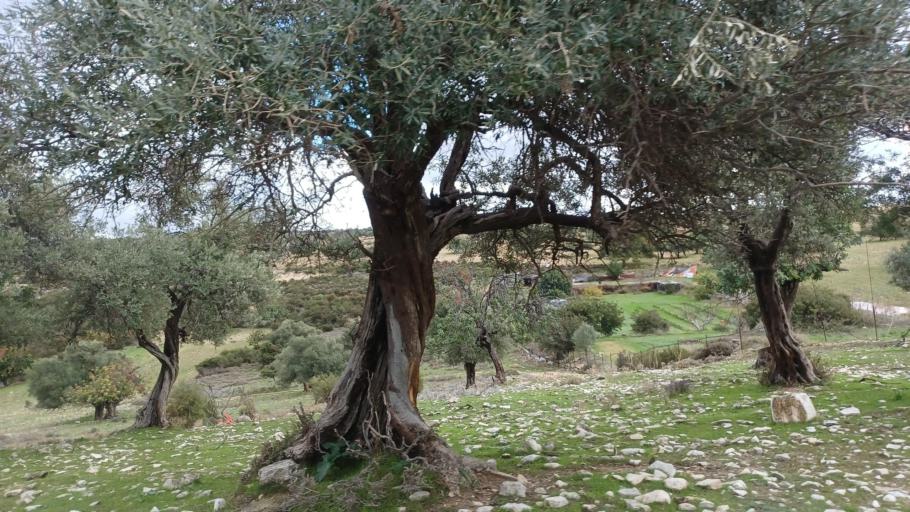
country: CY
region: Limassol
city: Sotira
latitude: 34.7262
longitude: 32.8246
